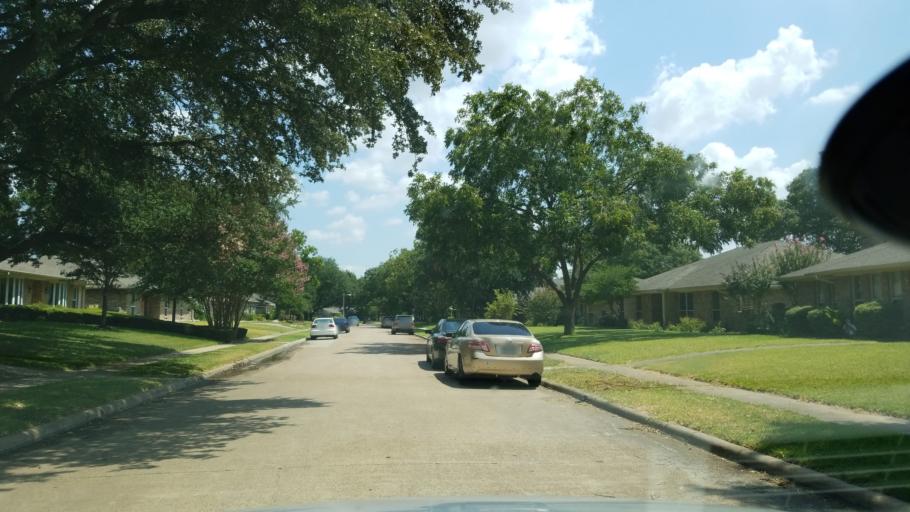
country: US
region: Texas
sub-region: Dallas County
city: Richardson
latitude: 32.9306
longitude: -96.7312
